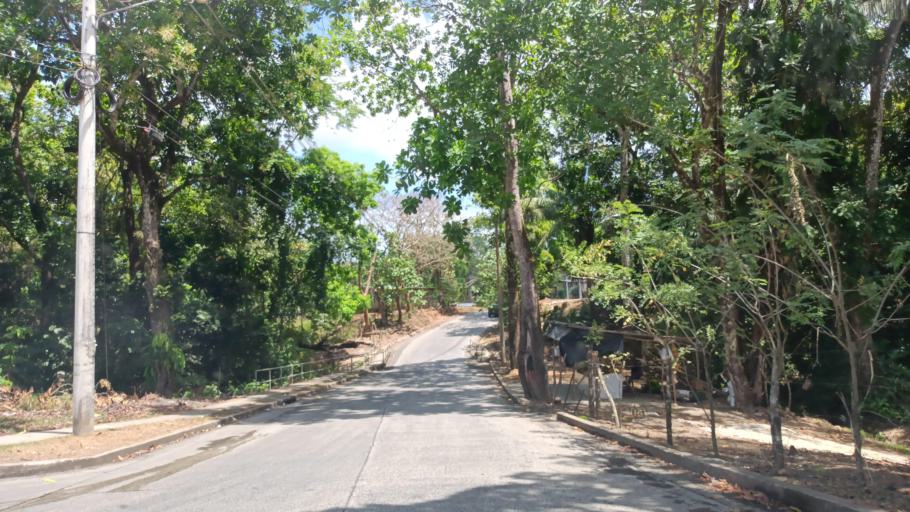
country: PA
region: Panama
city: Alcalde Diaz
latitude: 9.0994
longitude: -79.5673
